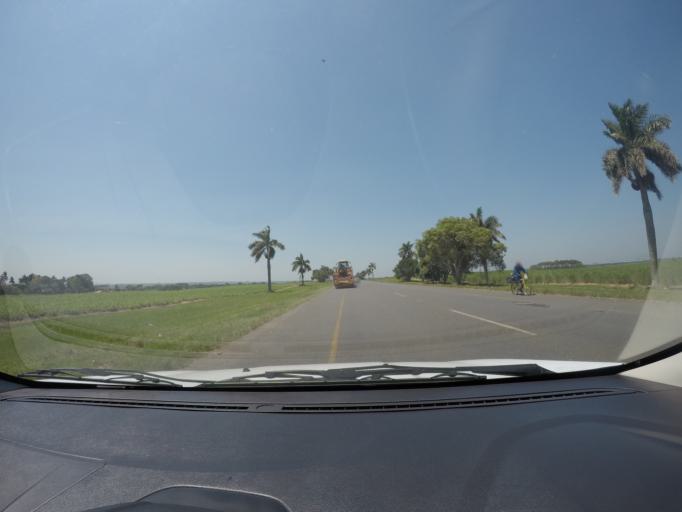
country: ZA
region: KwaZulu-Natal
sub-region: uThungulu District Municipality
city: Empangeni
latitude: -28.8121
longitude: 31.9555
